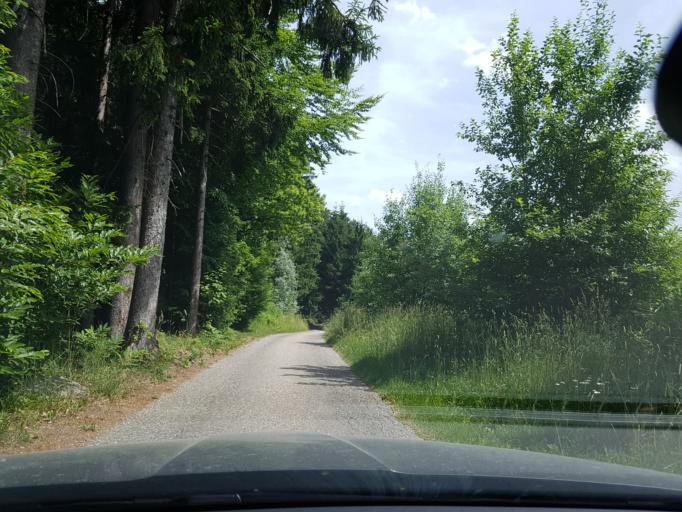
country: AT
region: Carinthia
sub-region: Politischer Bezirk Spittal an der Drau
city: Millstatt
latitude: 46.7773
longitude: 13.5563
